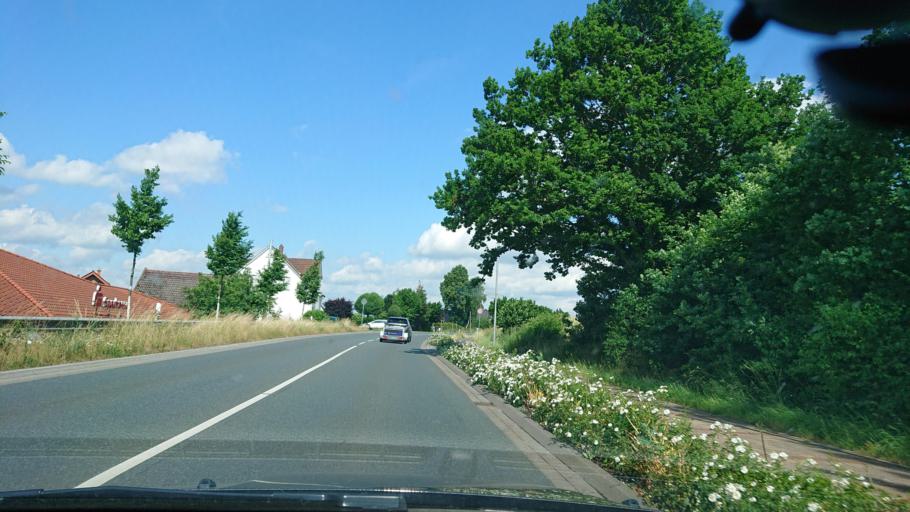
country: DE
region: North Rhine-Westphalia
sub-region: Regierungsbezirk Detmold
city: Herford
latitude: 52.1391
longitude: 8.6507
